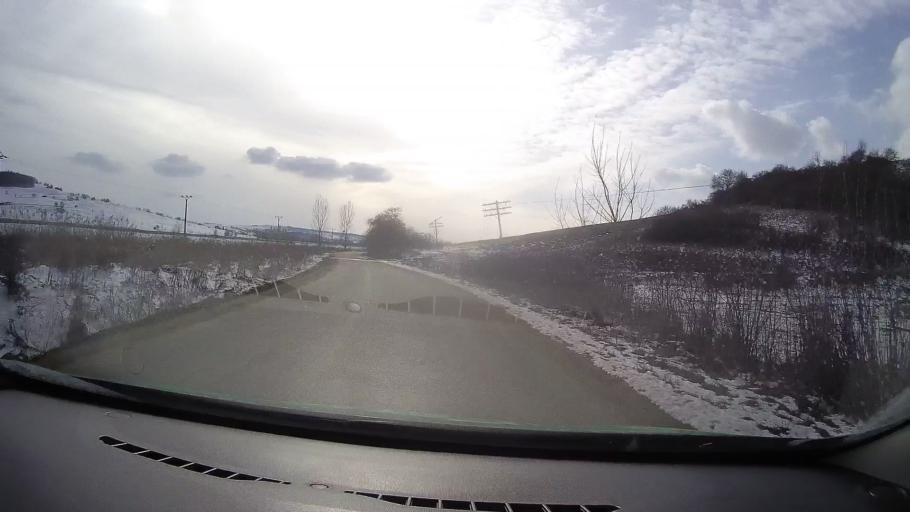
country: RO
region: Sibiu
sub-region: Comuna Bradeni
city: Bradeni
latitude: 46.0697
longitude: 24.8041
